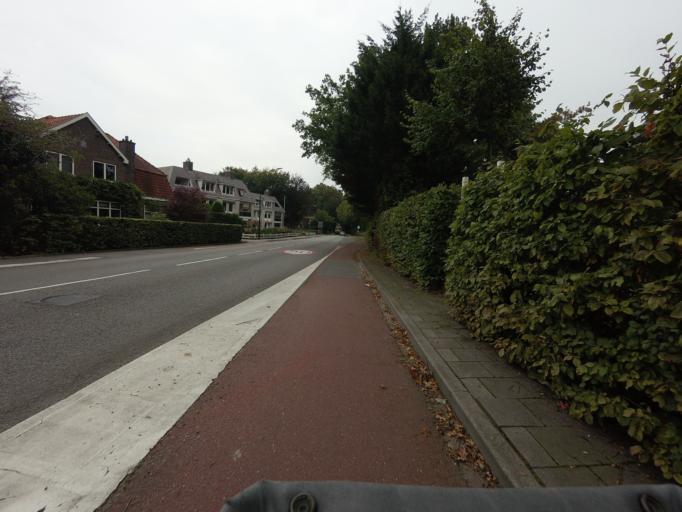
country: NL
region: North Holland
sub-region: Gemeente Wijdemeren
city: Nieuw-Loosdrecht
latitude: 52.2047
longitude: 5.1286
